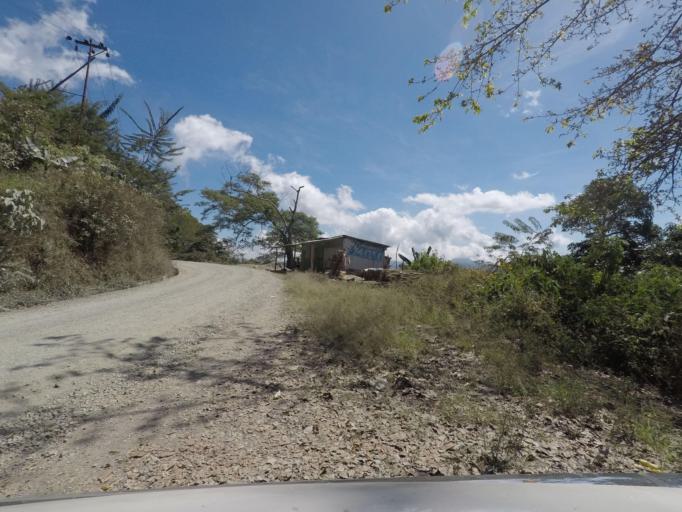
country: TL
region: Ermera
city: Gleno
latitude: -8.7461
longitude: 125.3934
